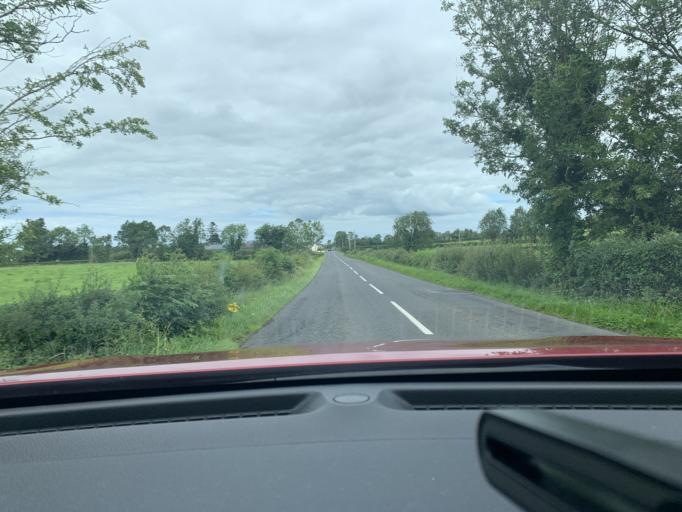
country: GB
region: Northern Ireland
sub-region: Fermanagh District
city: Enniskillen
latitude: 54.2738
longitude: -7.7037
